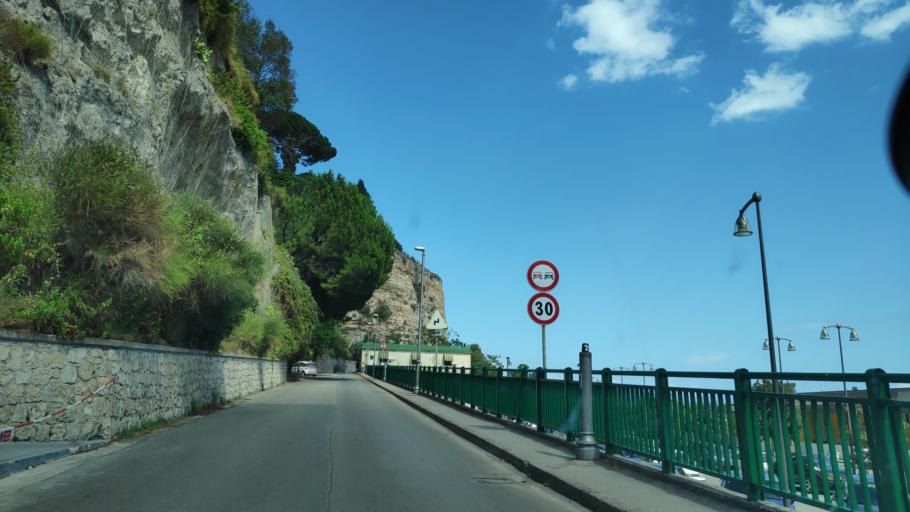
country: IT
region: Campania
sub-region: Provincia di Salerno
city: Vietri sul Mare
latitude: 40.6681
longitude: 14.7257
